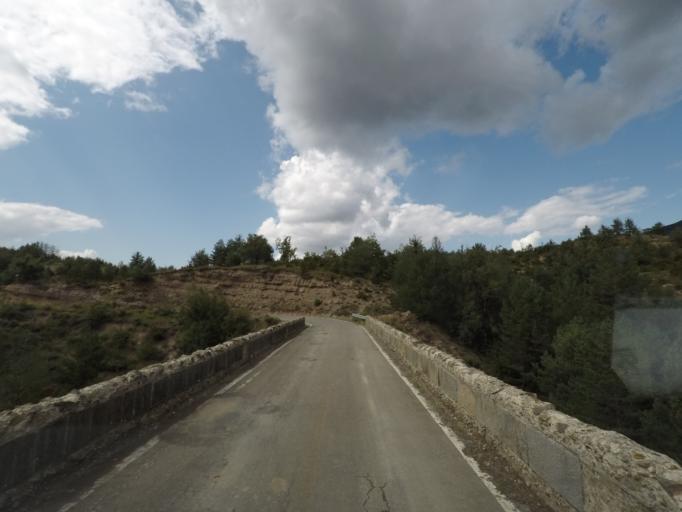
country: ES
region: Aragon
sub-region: Provincia de Huesca
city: Fiscal
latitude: 42.4080
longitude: -0.1400
